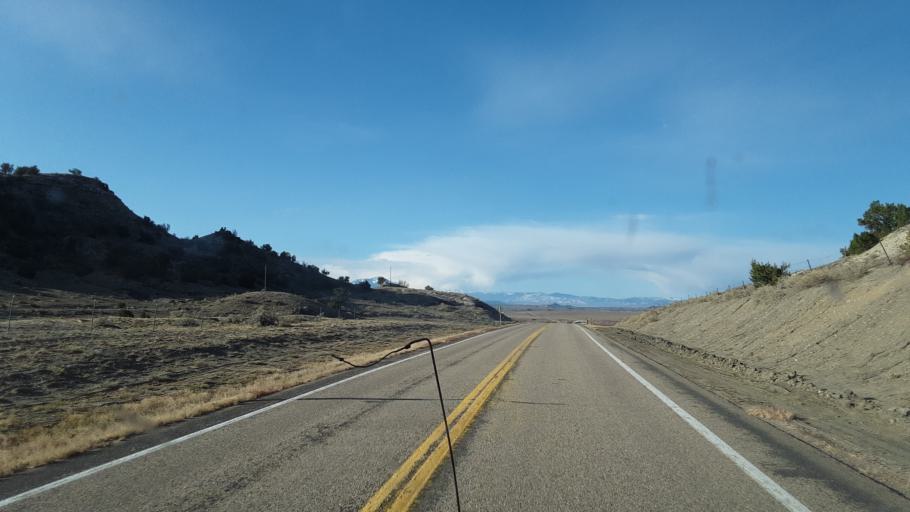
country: US
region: Colorado
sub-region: Huerfano County
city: Walsenburg
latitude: 37.6922
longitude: -104.6314
